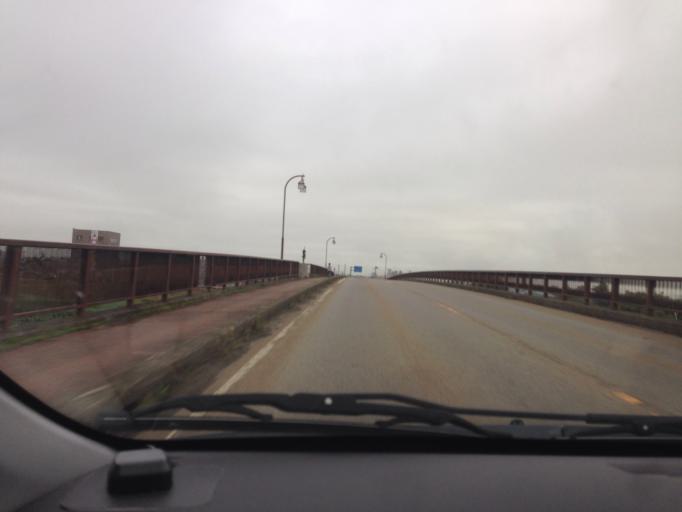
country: JP
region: Fukushima
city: Kitakata
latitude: 37.5891
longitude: 139.8928
